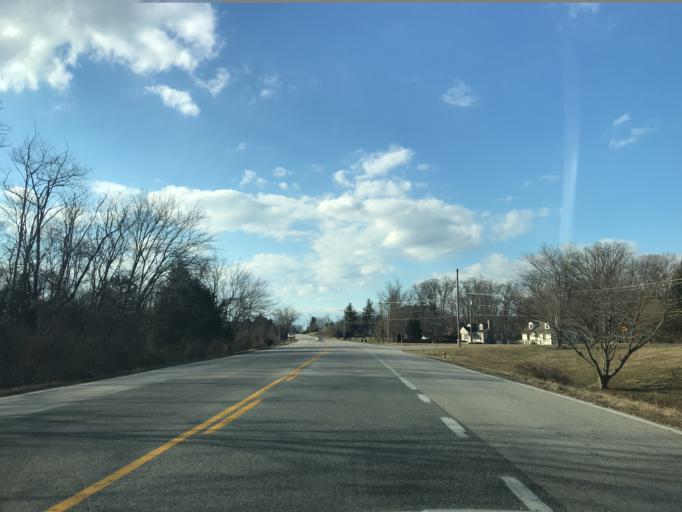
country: US
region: Maryland
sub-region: Cecil County
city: North East
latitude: 39.6442
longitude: -75.9651
